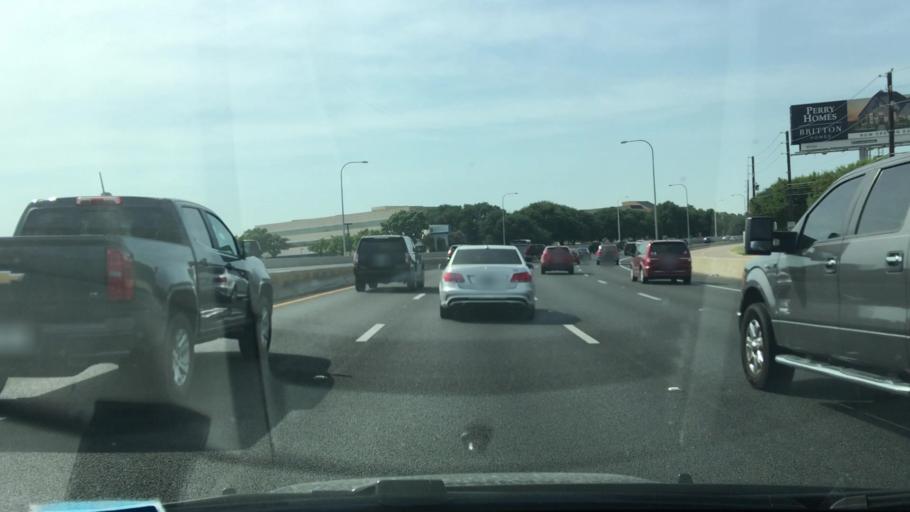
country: US
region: Texas
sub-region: Dallas County
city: Addison
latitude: 32.9785
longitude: -96.8273
